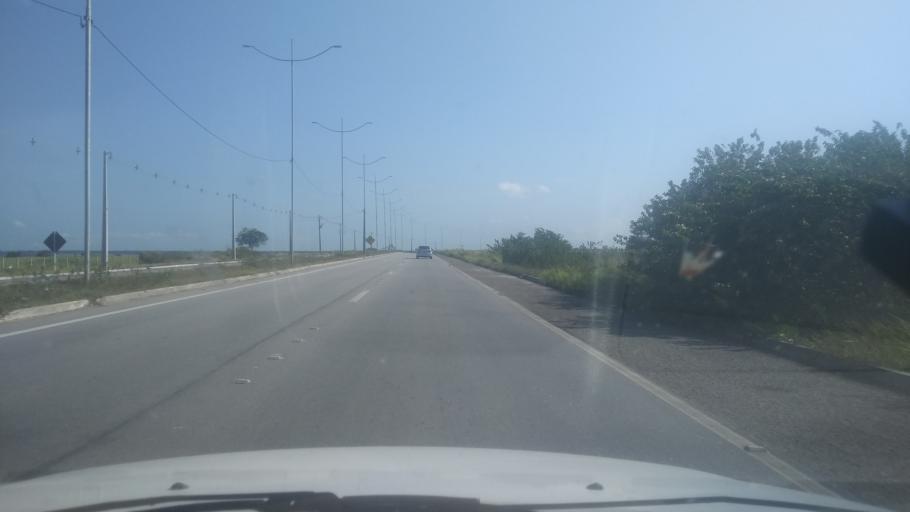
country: BR
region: Rio Grande do Norte
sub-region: Macaiba
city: Macaiba
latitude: -5.8285
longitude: -35.3700
